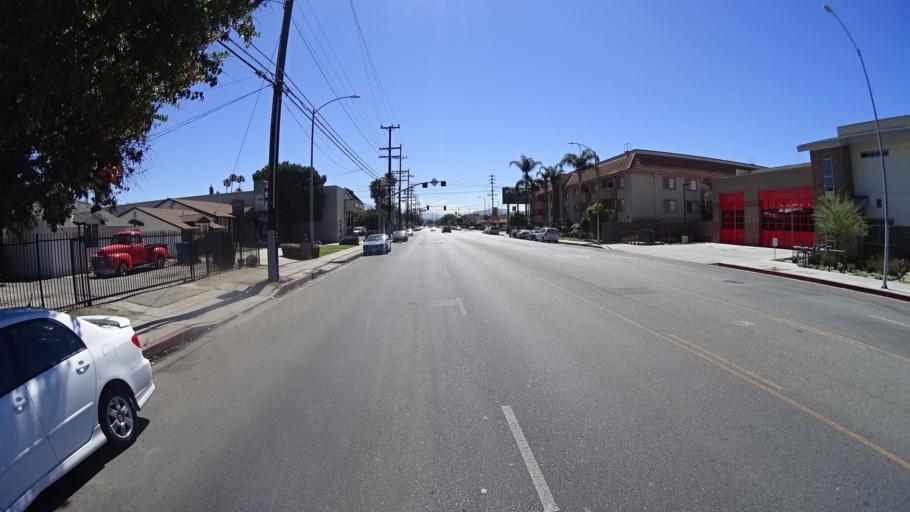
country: US
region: California
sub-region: Los Angeles County
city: San Fernando
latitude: 34.2427
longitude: -118.4516
